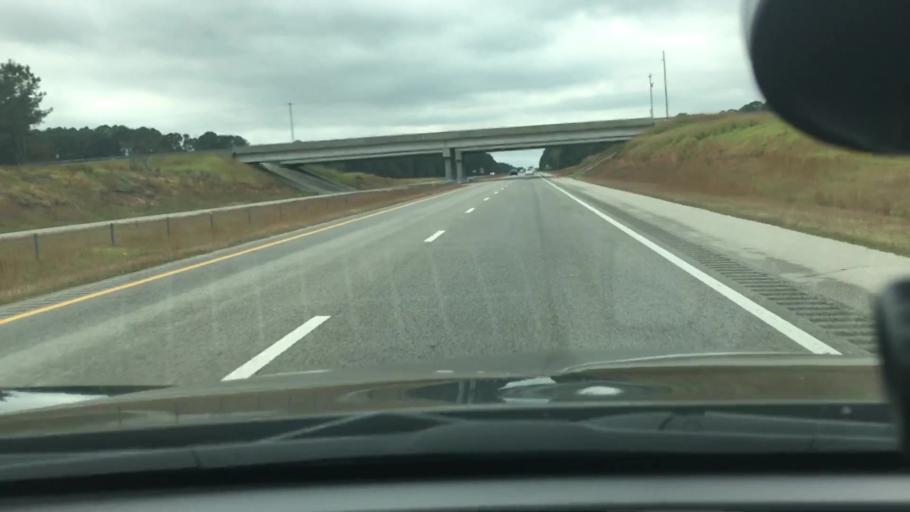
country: US
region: North Carolina
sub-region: Wilson County
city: Wilson
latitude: 35.6753
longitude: -77.8567
